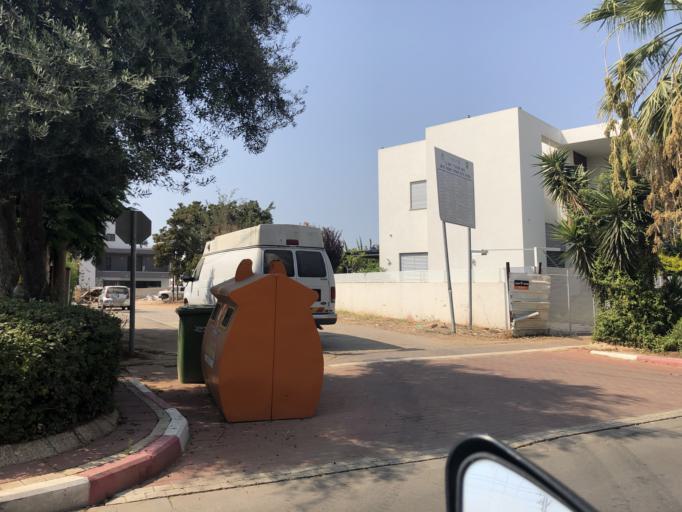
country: IL
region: Tel Aviv
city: Bene Beraq
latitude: 32.0555
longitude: 34.8324
